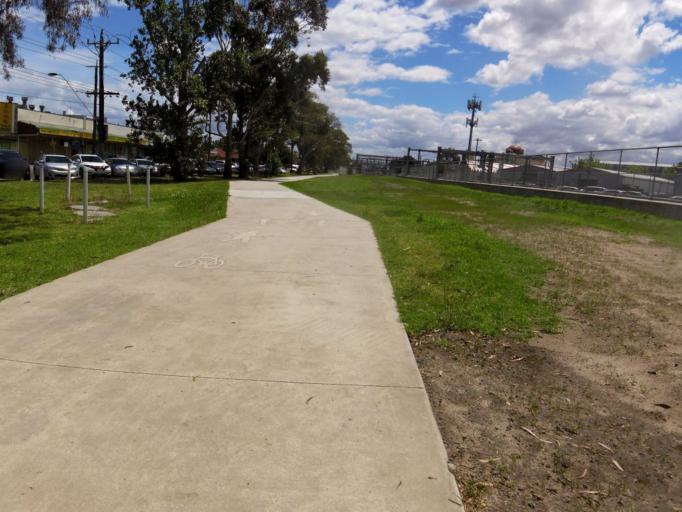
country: AU
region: Victoria
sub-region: Greater Dandenong
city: Springvale
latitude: -37.9484
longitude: 145.1519
